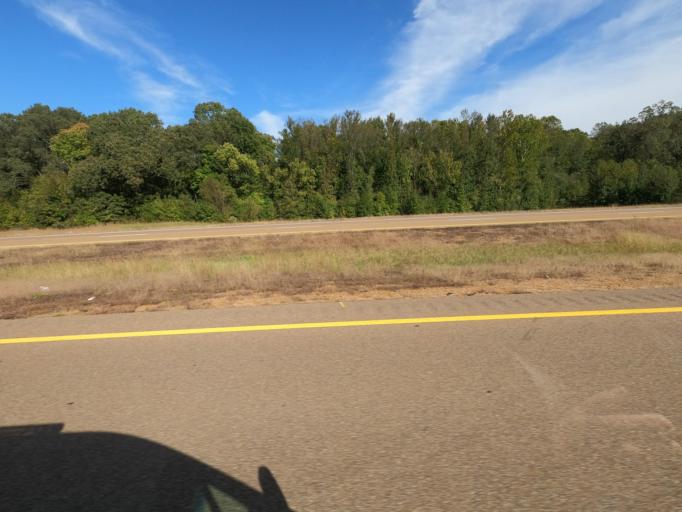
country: US
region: Tennessee
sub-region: Fayette County
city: Piperton
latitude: 35.1332
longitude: -89.6398
